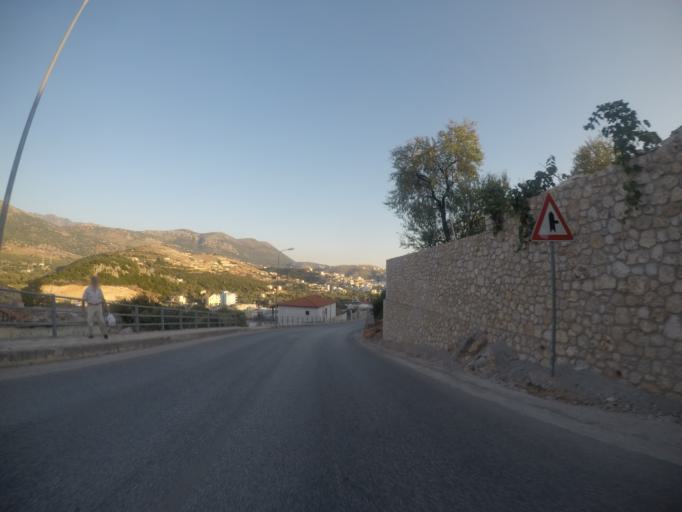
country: AL
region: Vlore
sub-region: Rrethi i Vlores
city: Himare
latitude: 40.1111
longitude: 19.7396
